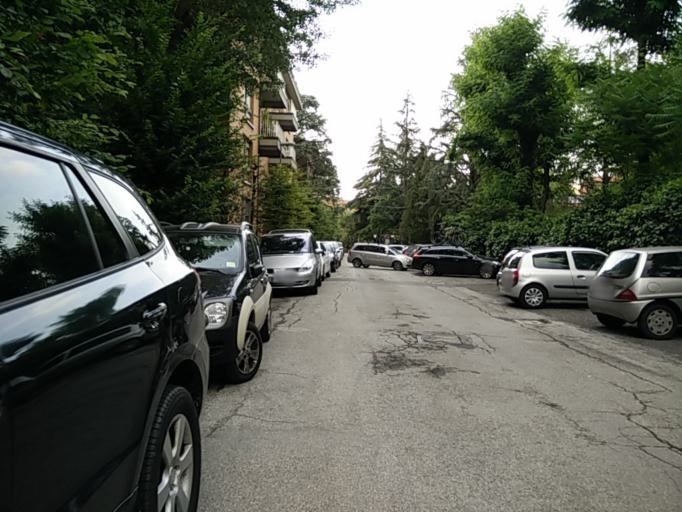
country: IT
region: Emilia-Romagna
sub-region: Provincia di Bologna
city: Casalecchio di Reno
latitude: 44.4752
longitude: 11.2831
